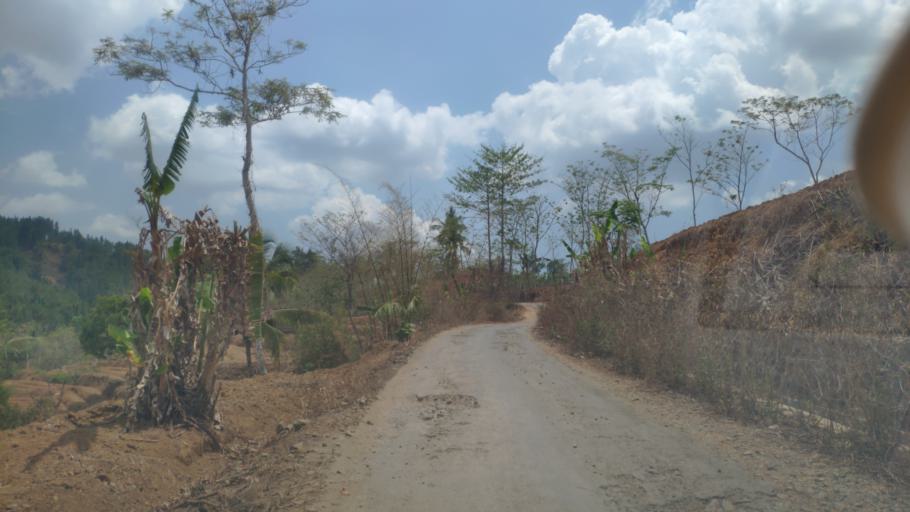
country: ID
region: Central Java
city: Gombong
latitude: -7.4730
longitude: 109.6116
